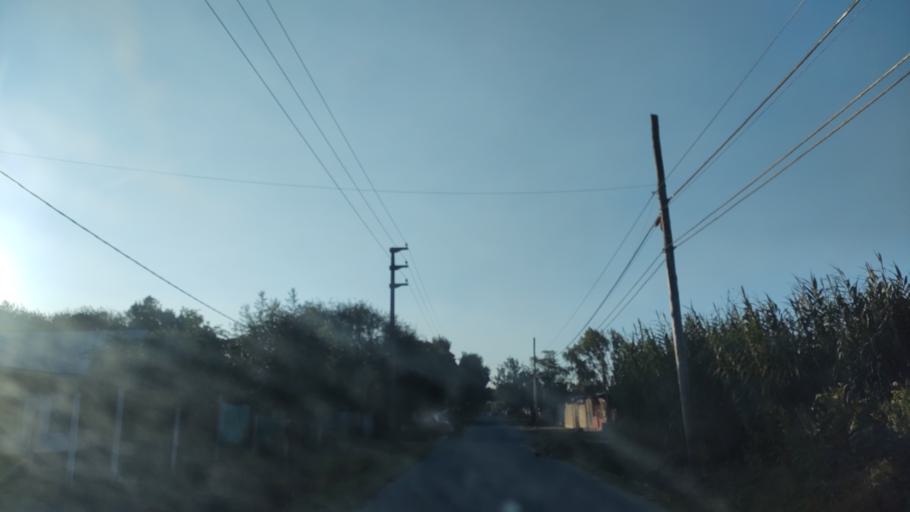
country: AR
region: Buenos Aires
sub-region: Partido de La Plata
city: La Plata
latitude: -34.9692
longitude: -57.9760
